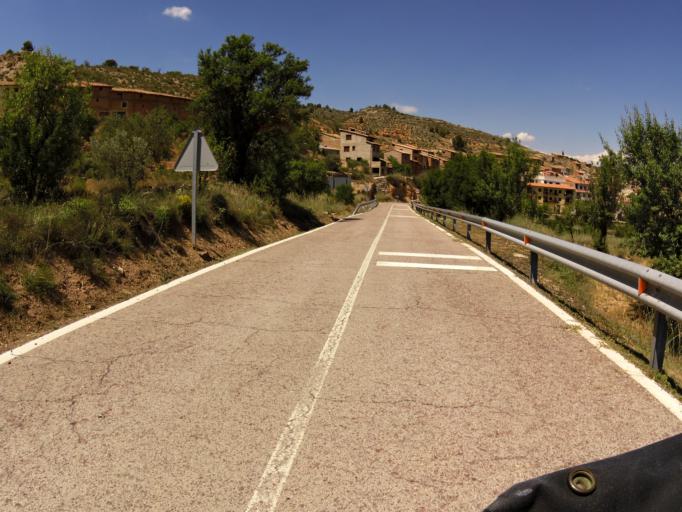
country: ES
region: Valencia
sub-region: Provincia de Valencia
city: Casas Bajas
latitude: 40.0209
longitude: -1.2642
